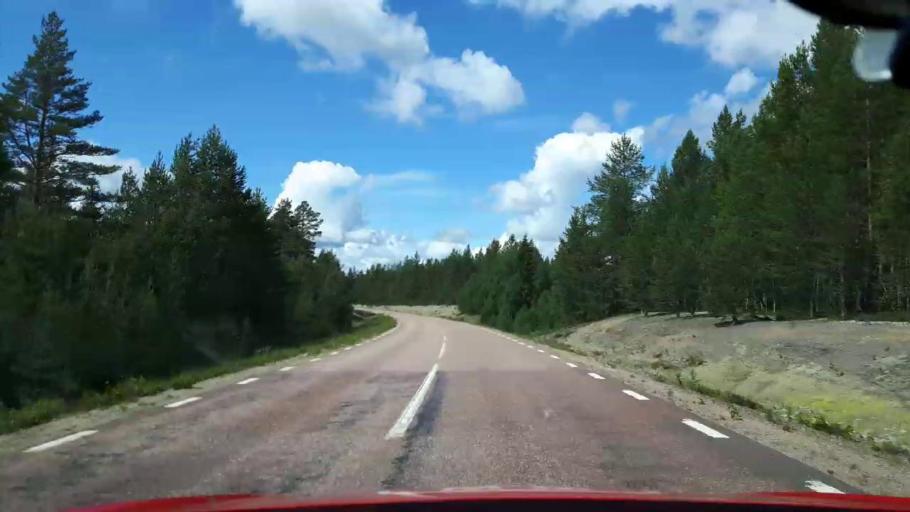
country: SE
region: Dalarna
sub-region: Alvdalens Kommun
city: AElvdalen
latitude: 61.8054
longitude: 13.6508
